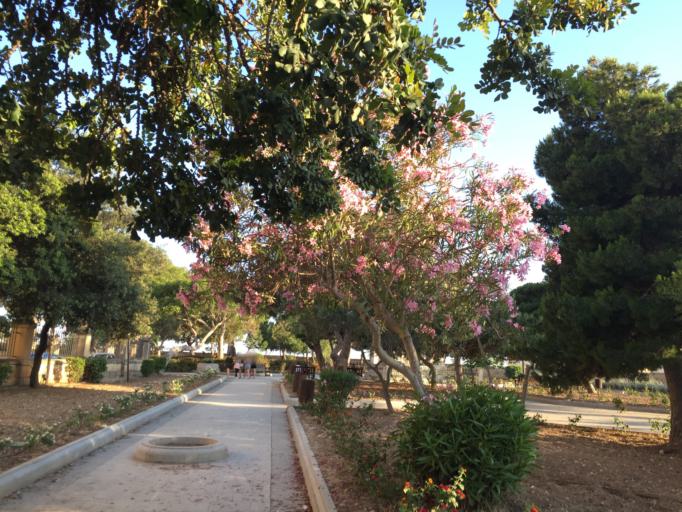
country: MT
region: Il-Furjana
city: Floriana
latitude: 35.8974
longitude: 14.5082
